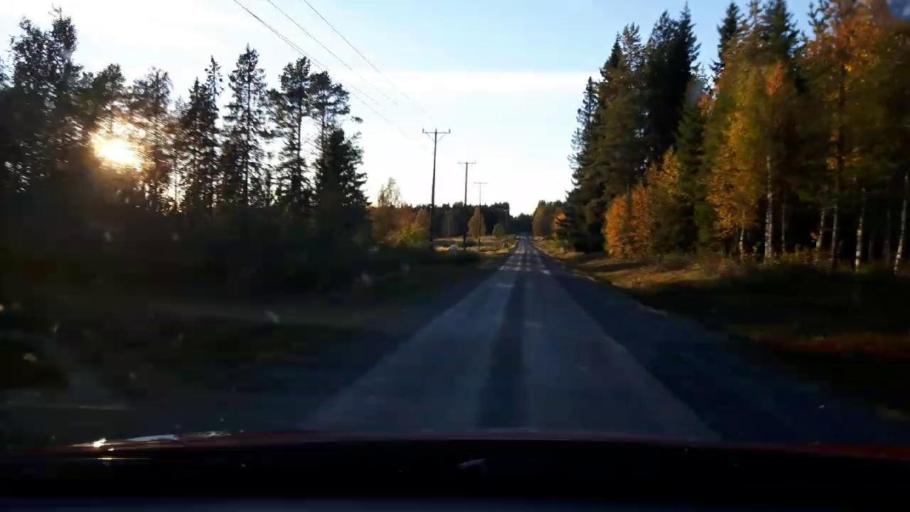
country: SE
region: Jaemtland
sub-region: Krokoms Kommun
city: Krokom
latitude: 63.4307
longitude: 14.4390
